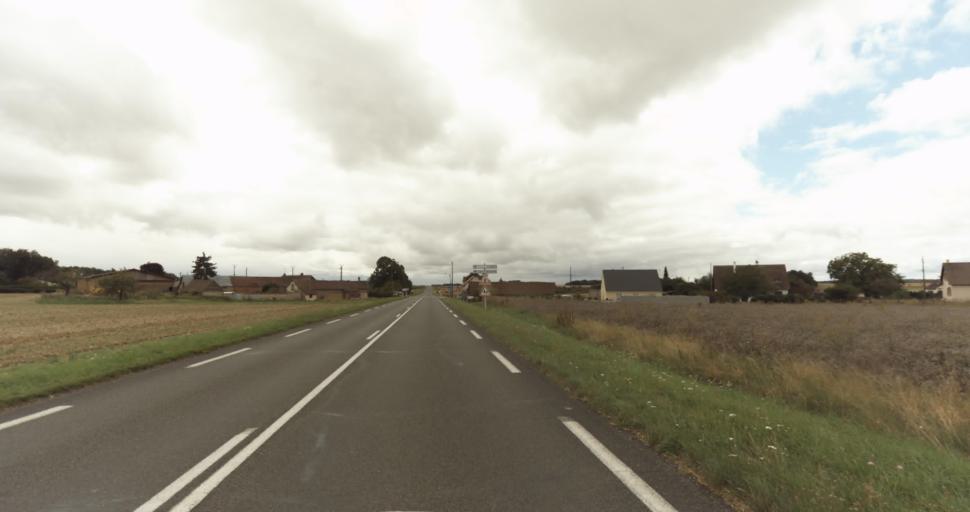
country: FR
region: Haute-Normandie
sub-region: Departement de l'Eure
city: Evreux
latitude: 48.9550
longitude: 1.1620
